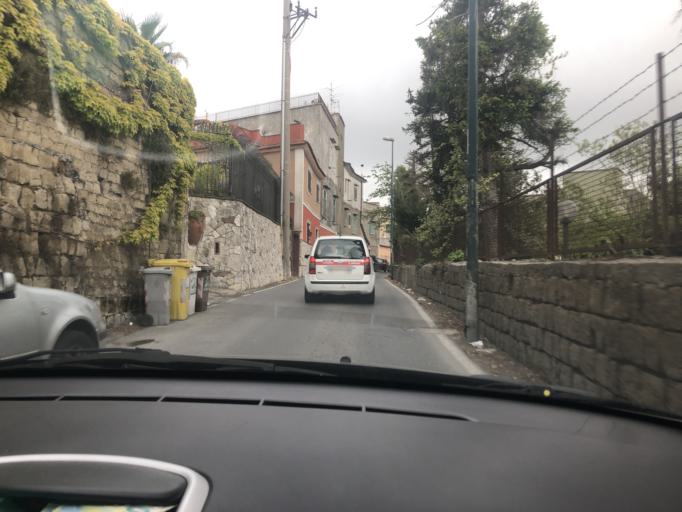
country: IT
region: Campania
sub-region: Provincia di Napoli
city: Torre Caracciolo
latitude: 40.8663
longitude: 14.1886
